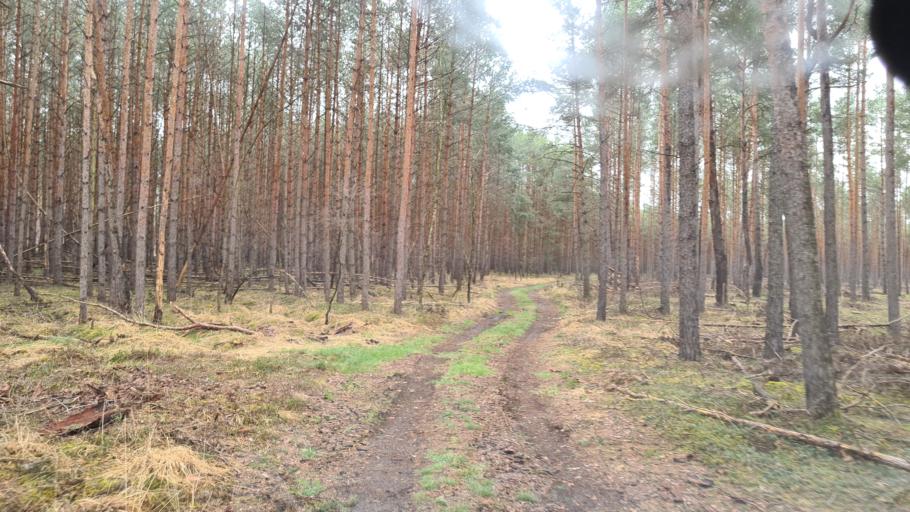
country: DE
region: Brandenburg
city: Schonewalde
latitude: 51.6475
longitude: 13.6293
